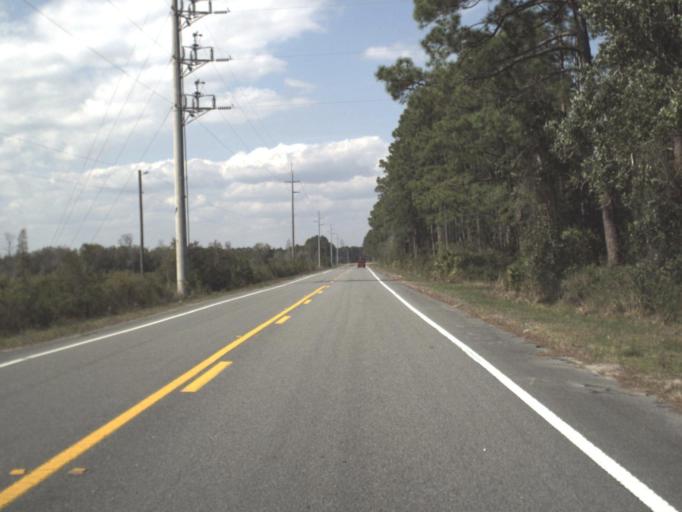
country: US
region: Florida
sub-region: Franklin County
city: Carrabelle
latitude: 29.9443
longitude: -84.5012
